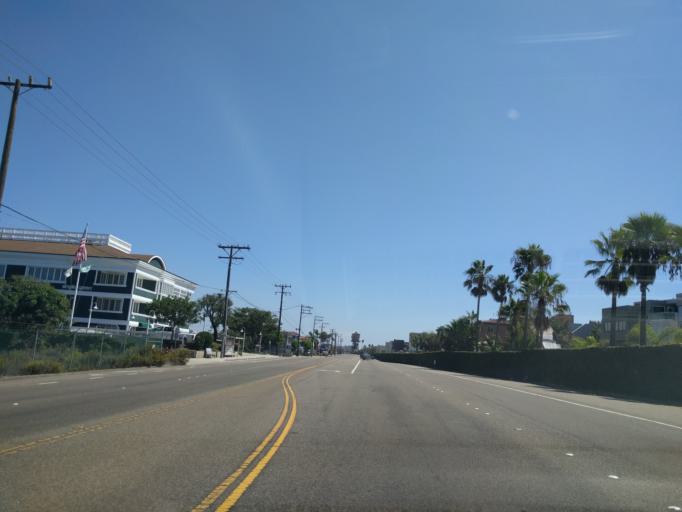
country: US
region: California
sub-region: Orange County
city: Seal Beach
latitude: 33.7284
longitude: -118.0831
